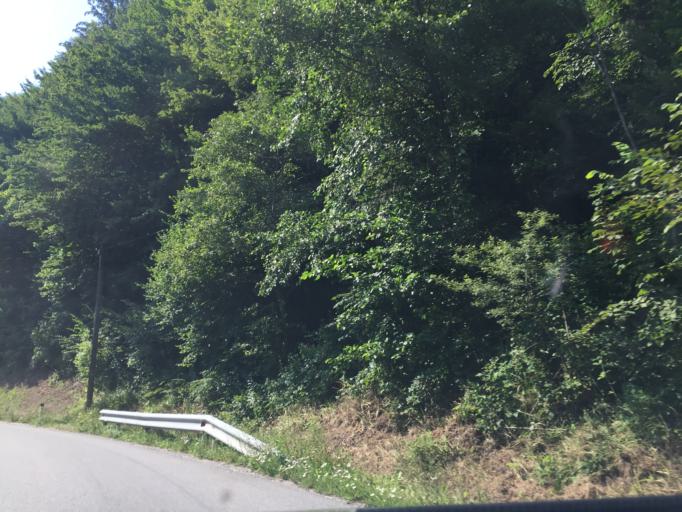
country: SI
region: Radlje ob Dravi
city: Radlje ob Dravi
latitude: 46.6390
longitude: 15.2156
